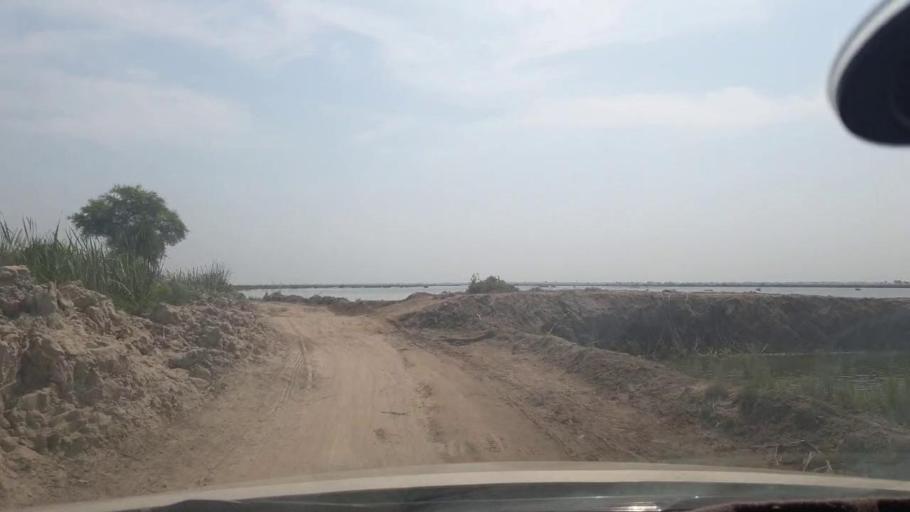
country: PK
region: Sindh
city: Jacobabad
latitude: 28.3104
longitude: 68.4794
